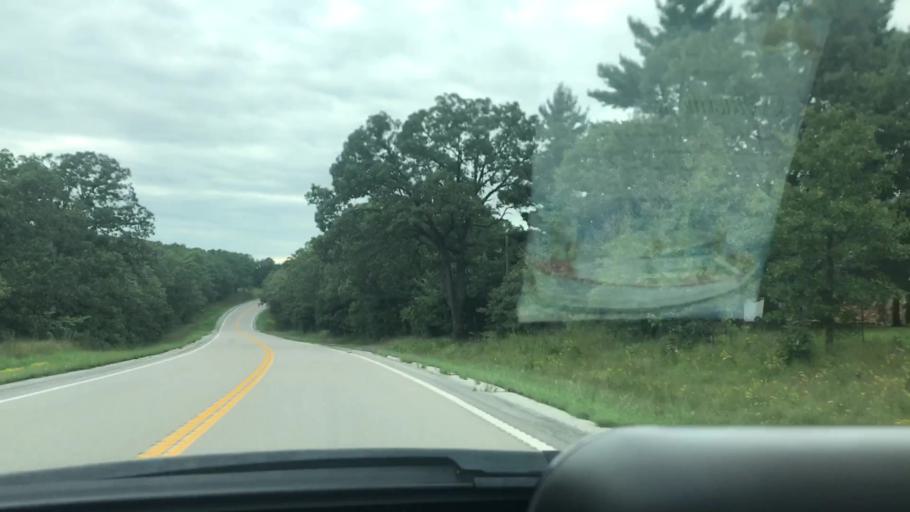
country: US
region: Missouri
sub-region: Benton County
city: Warsaw
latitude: 38.1619
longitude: -93.3003
